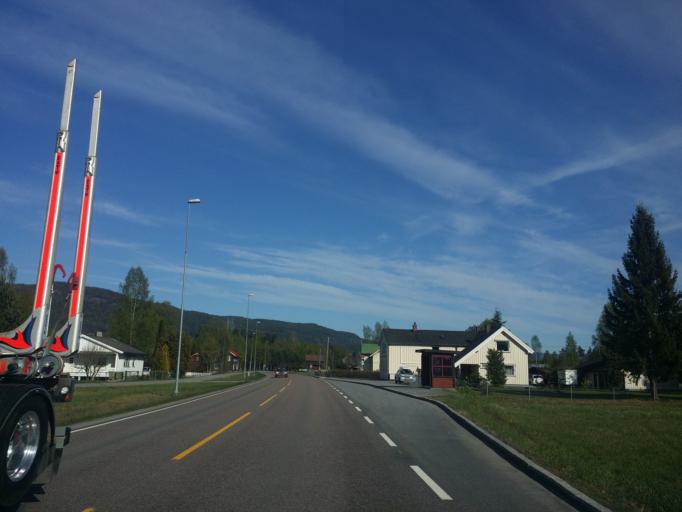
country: NO
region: Telemark
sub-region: Notodden
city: Notodden
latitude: 59.5966
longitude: 9.1349
